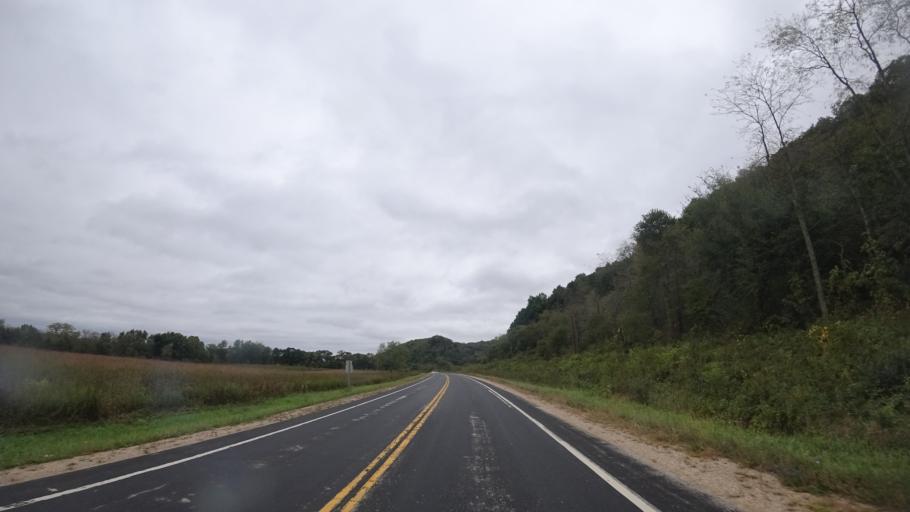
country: US
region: Wisconsin
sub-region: Grant County
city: Boscobel
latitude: 43.2047
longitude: -90.6438
